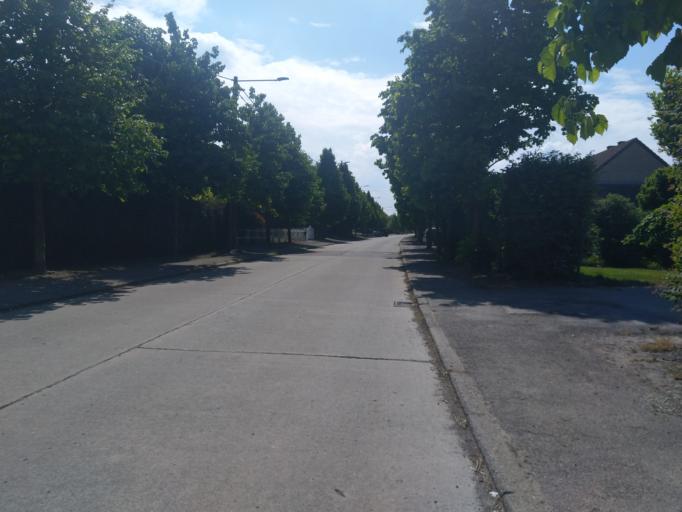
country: BE
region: Wallonia
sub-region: Province du Hainaut
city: Chasse Royale
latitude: 50.4285
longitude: 3.9945
